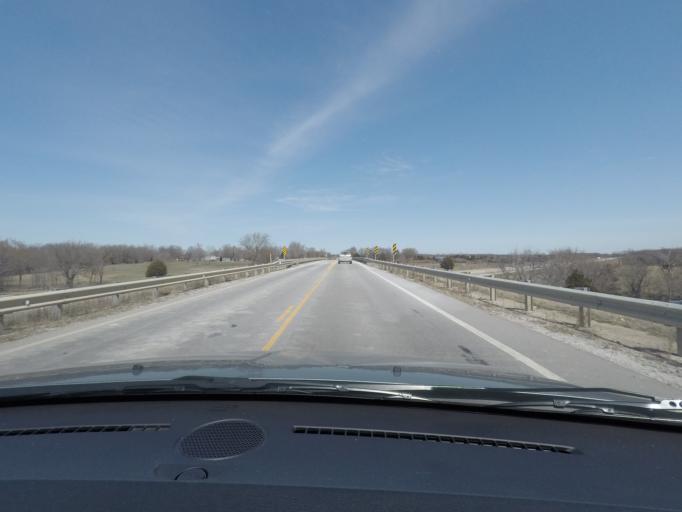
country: US
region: Kansas
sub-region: Lyon County
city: Emporia
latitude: 38.4840
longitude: -96.1709
